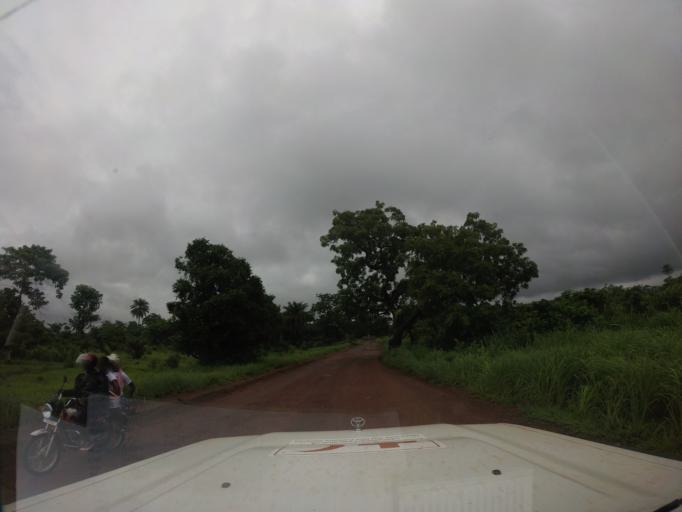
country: SL
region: Northern Province
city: Kambia
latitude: 9.1290
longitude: -12.9005
